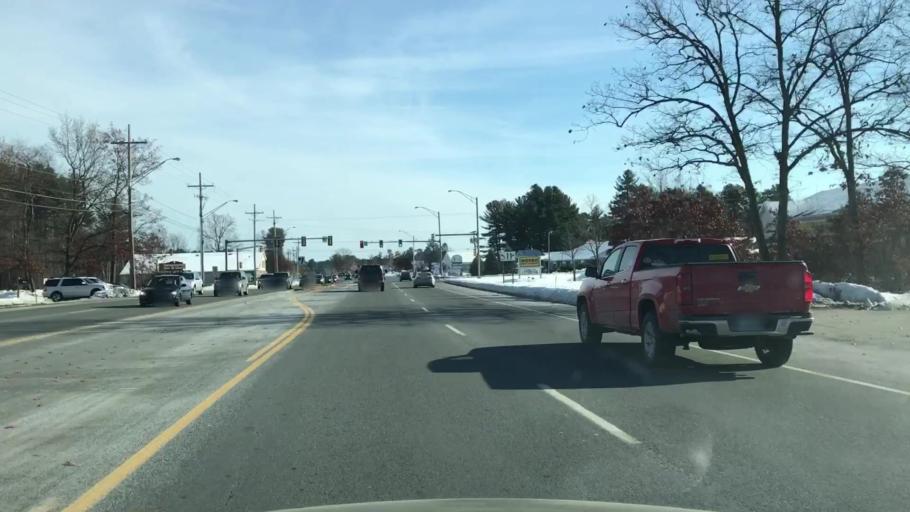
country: US
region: New Hampshire
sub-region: Hillsborough County
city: Hollis
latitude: 42.8100
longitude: -71.5746
